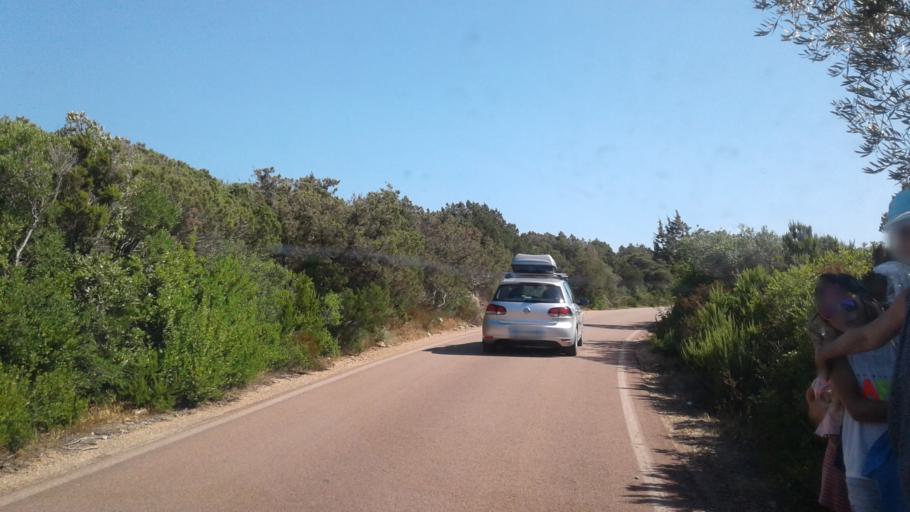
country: IT
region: Sardinia
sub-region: Provincia di Olbia-Tempio
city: La Maddalena
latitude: 41.1865
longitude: 9.4565
